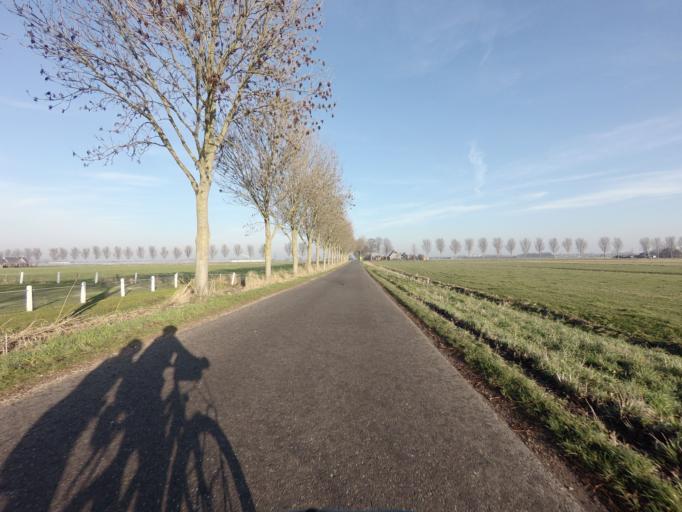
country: NL
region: Utrecht
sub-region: Gemeente De Ronde Venen
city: Mijdrecht
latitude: 52.1999
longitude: 4.8274
